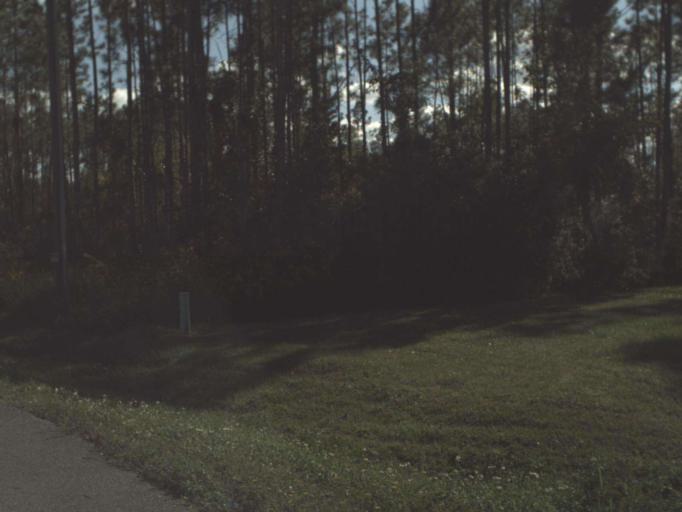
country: US
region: Florida
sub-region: Gulf County
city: Wewahitchka
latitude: 30.0430
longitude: -85.1852
